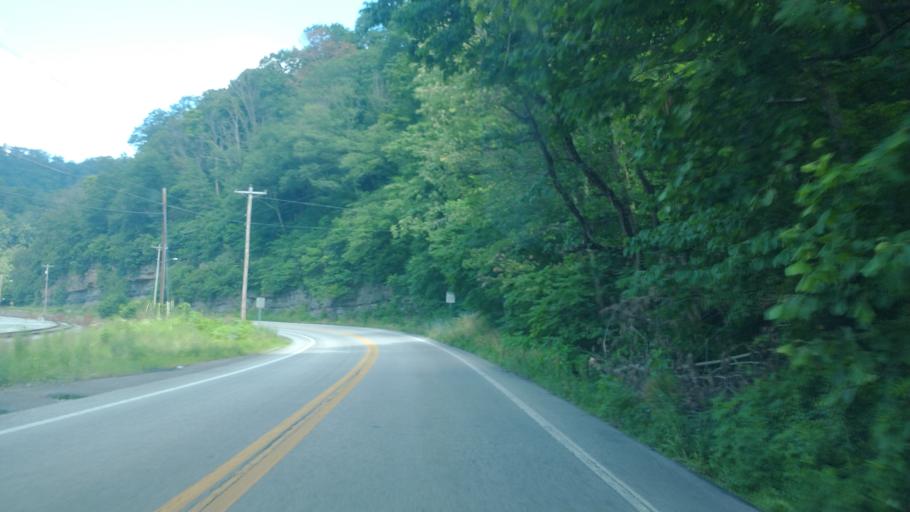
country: US
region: West Virginia
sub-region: McDowell County
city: Welch
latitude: 37.4243
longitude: -81.5017
